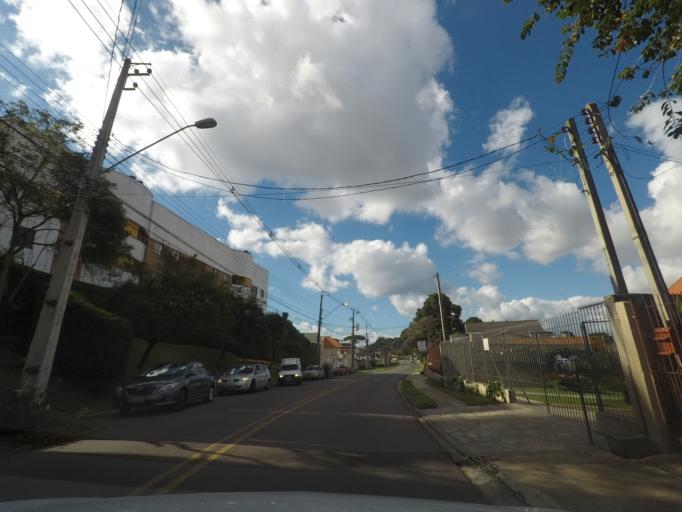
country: BR
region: Parana
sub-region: Curitiba
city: Curitiba
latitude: -25.3788
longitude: -49.2788
